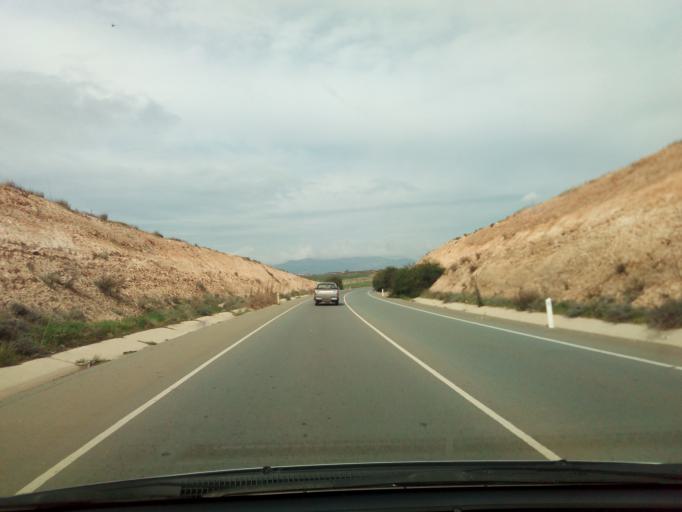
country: CY
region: Lefkosia
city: Akaki
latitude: 35.1534
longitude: 33.1553
